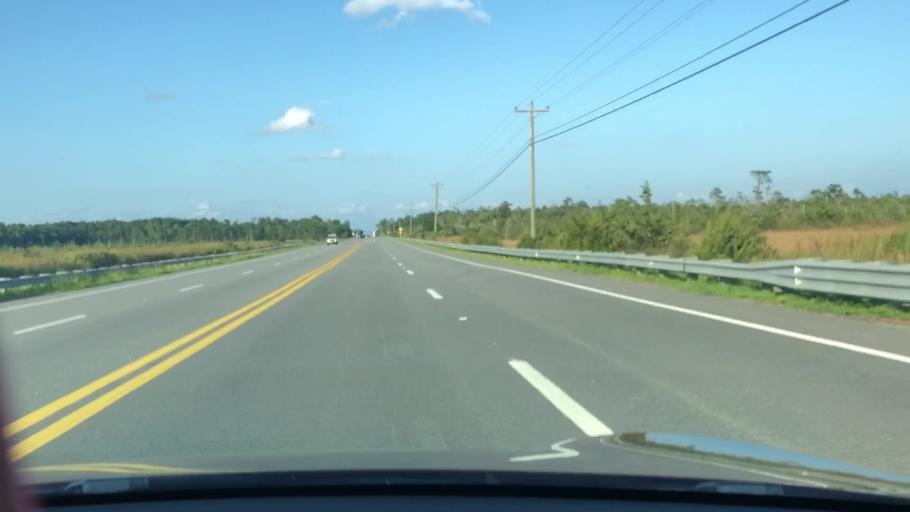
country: US
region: North Carolina
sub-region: Dare County
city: Manteo
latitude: 35.8805
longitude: -75.7746
